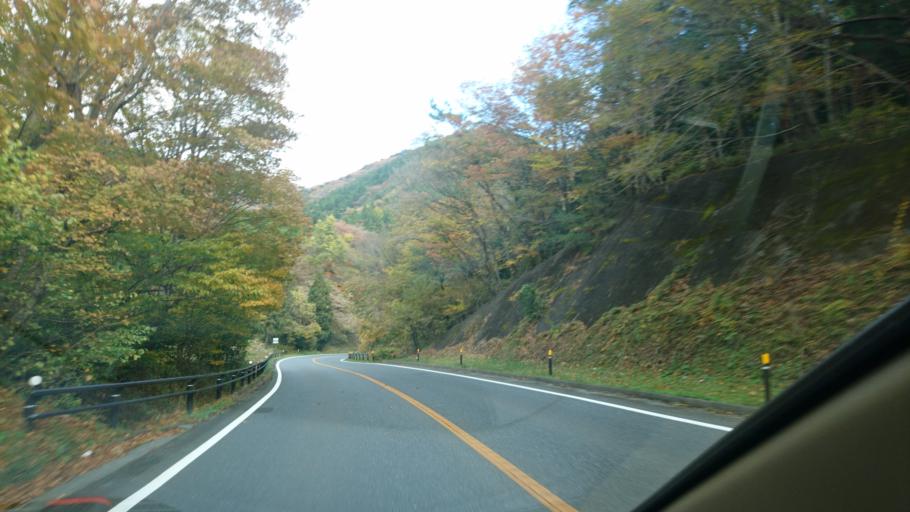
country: JP
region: Iwate
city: Ofunato
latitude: 39.0270
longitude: 141.6956
